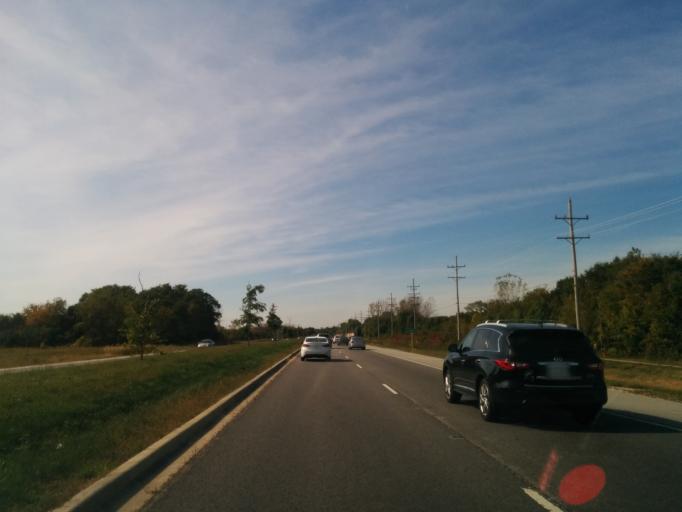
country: US
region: Illinois
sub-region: DuPage County
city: Wheaton
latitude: 41.8289
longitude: -88.1121
